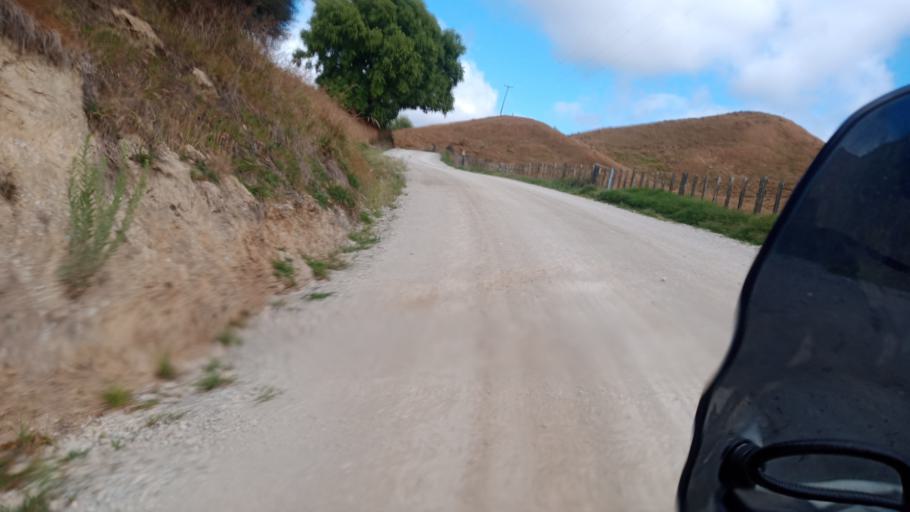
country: NZ
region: Hawke's Bay
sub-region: Wairoa District
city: Wairoa
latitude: -38.6050
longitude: 177.4959
